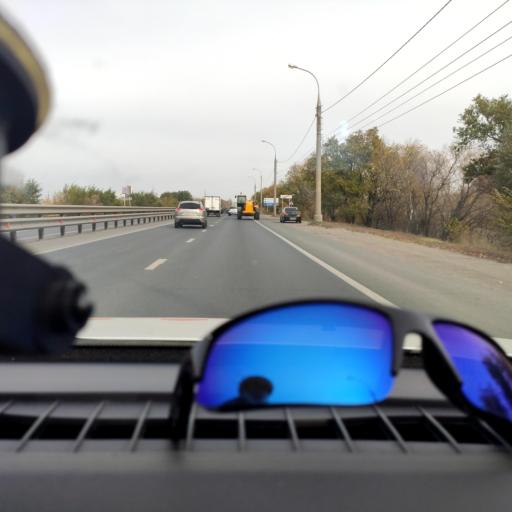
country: RU
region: Samara
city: Samara
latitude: 53.1208
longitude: 50.1690
